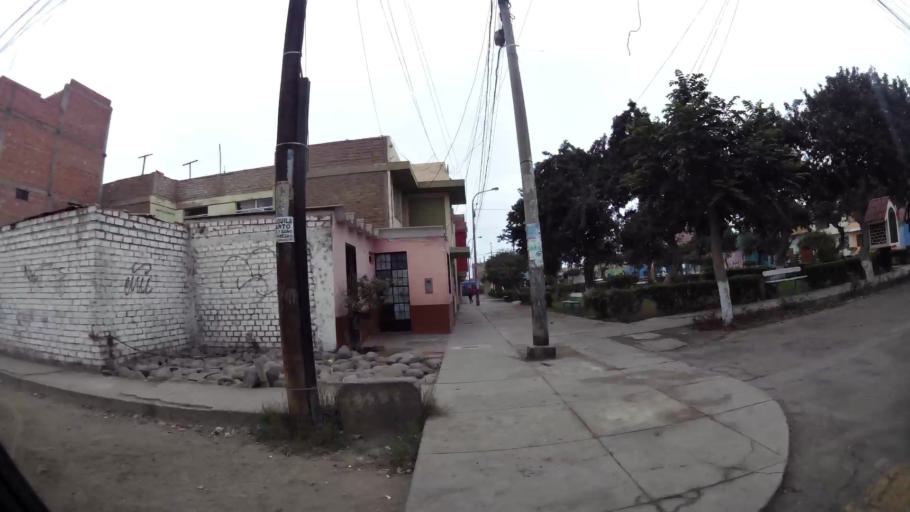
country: PE
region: Lima
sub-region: Barranca
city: Barranca
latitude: -10.7494
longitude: -77.7659
